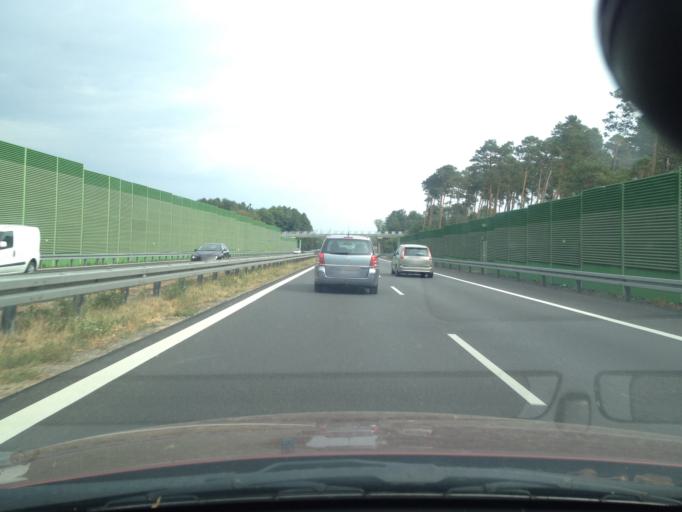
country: PL
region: Lubusz
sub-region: Zielona Gora
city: Zielona Gora
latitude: 51.9860
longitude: 15.5697
